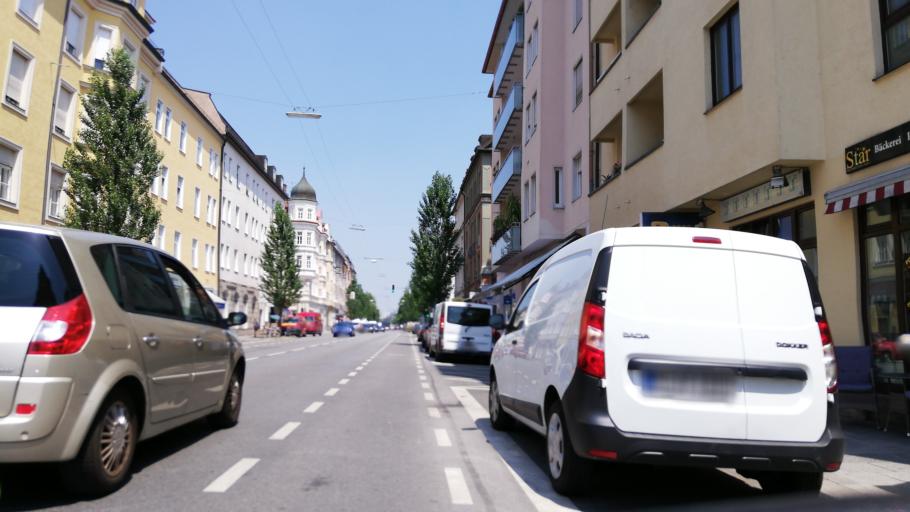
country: DE
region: Bavaria
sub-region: Upper Bavaria
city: Munich
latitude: 48.1563
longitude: 11.5620
